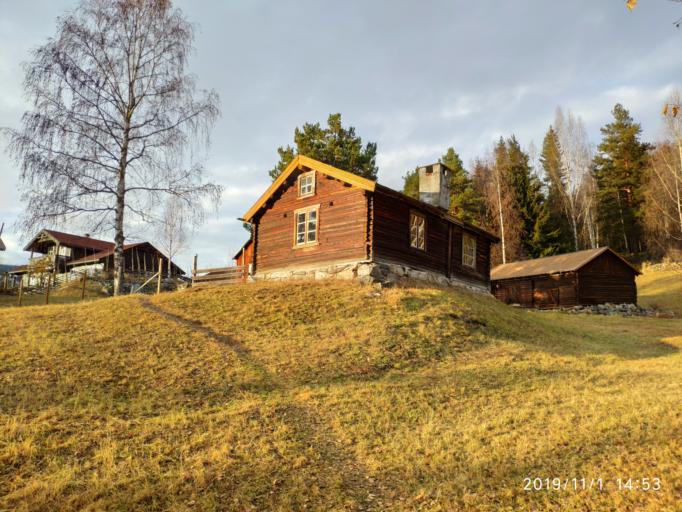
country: NO
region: Buskerud
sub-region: Gol
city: Gol
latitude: 60.7080
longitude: 8.9398
